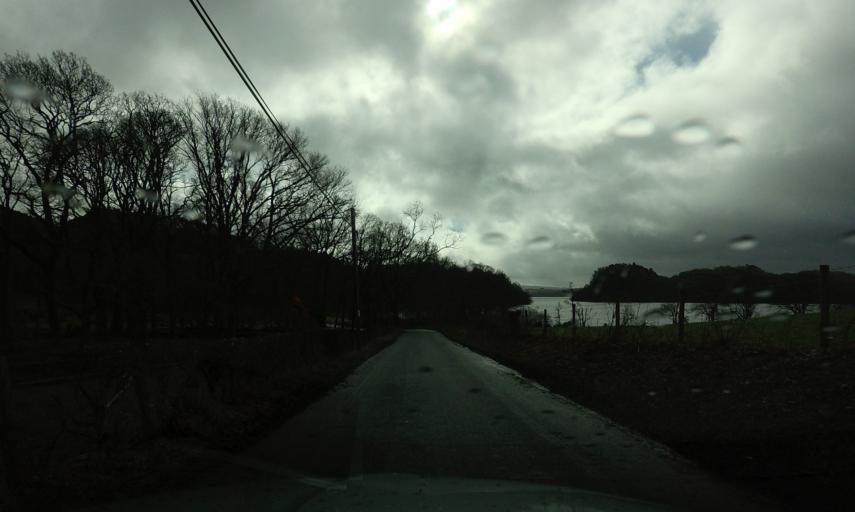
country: GB
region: Scotland
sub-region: West Dunbartonshire
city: Balloch
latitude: 56.0905
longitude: -4.5497
